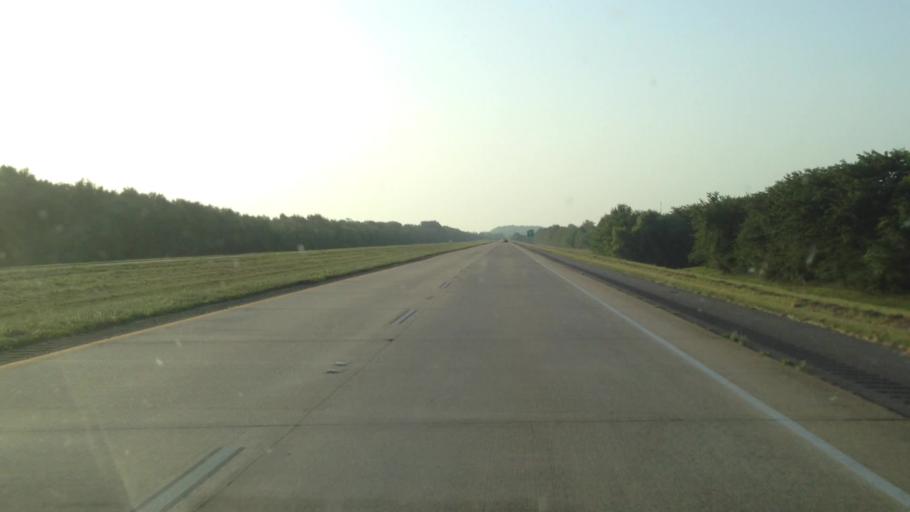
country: US
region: Louisiana
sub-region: Grant Parish
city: Colfax
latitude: 31.5071
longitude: -92.8870
